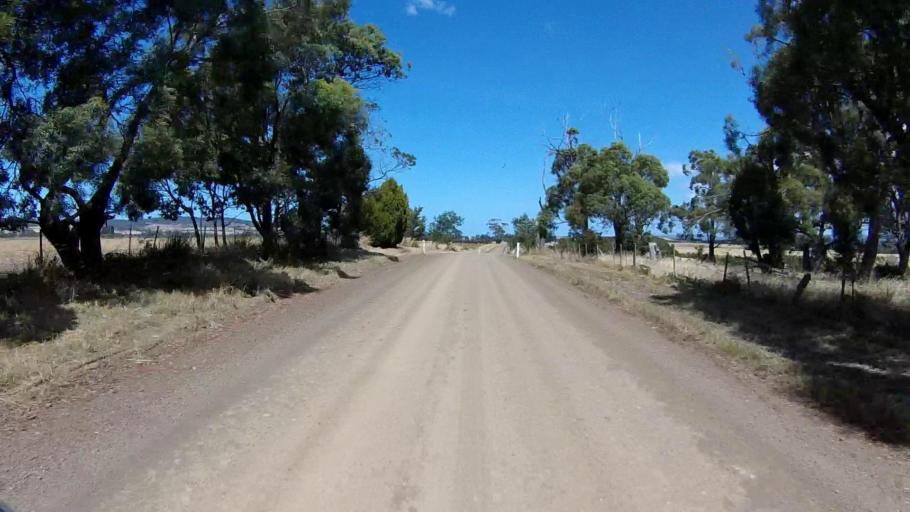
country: AU
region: Tasmania
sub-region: Break O'Day
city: St Helens
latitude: -41.9921
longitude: 148.0670
